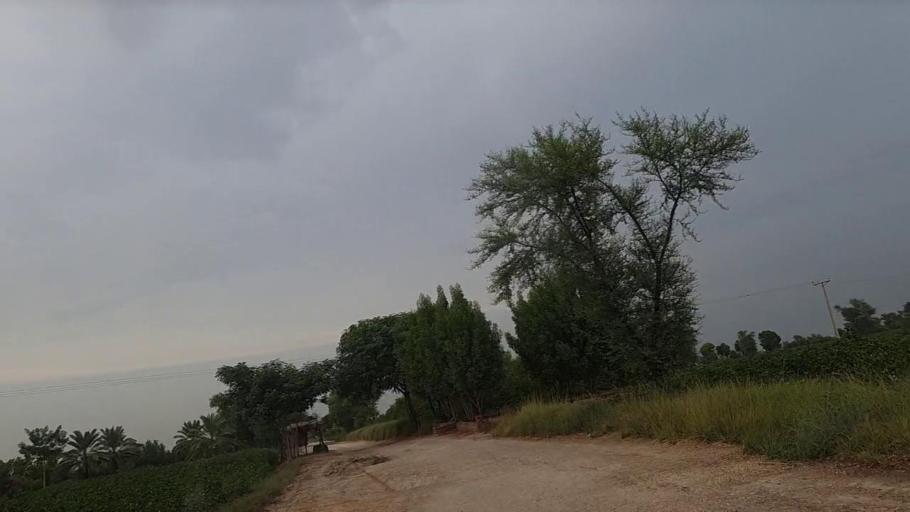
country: PK
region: Sindh
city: Karaundi
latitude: 26.9597
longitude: 68.3437
